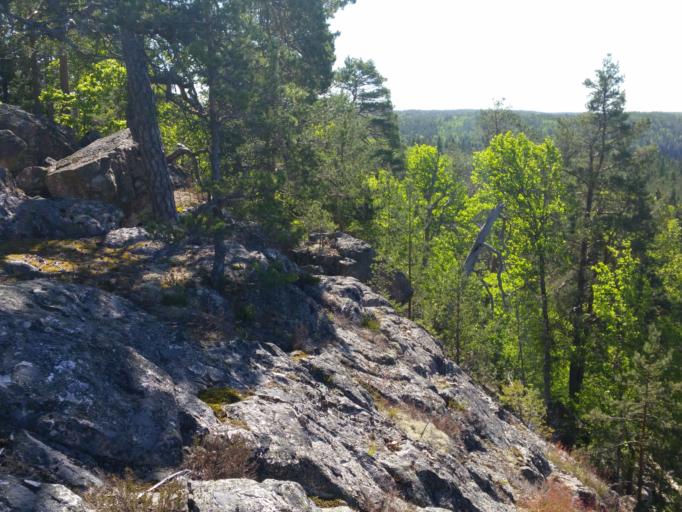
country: SE
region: Soedermanland
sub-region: Strangnas Kommun
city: Akers Styckebruk
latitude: 59.2068
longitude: 17.1551
